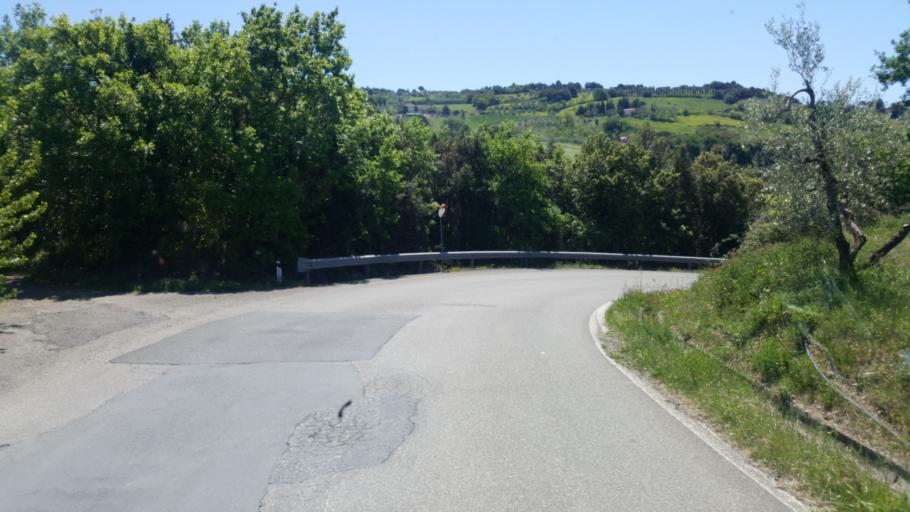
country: IT
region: Tuscany
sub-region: Province of Pisa
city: Castellina Marittima
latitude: 43.4244
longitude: 10.5448
